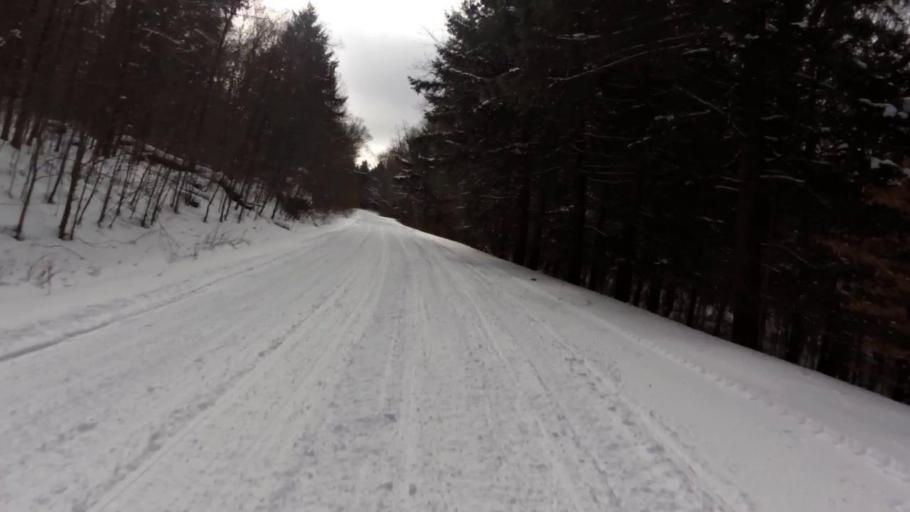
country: US
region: New York
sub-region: Cattaraugus County
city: Salamanca
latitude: 42.0741
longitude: -78.7538
